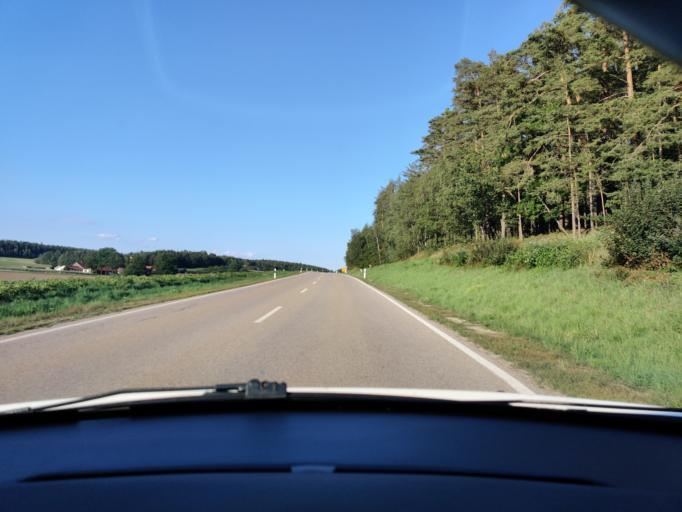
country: DE
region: Bavaria
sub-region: Upper Palatinate
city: Stulln
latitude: 49.4409
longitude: 12.1508
